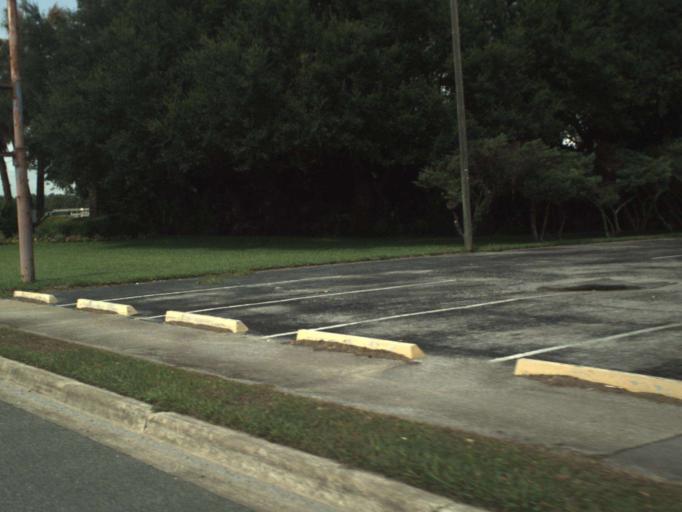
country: US
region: Florida
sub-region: Sumter County
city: Wildwood
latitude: 28.8596
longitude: -82.0425
